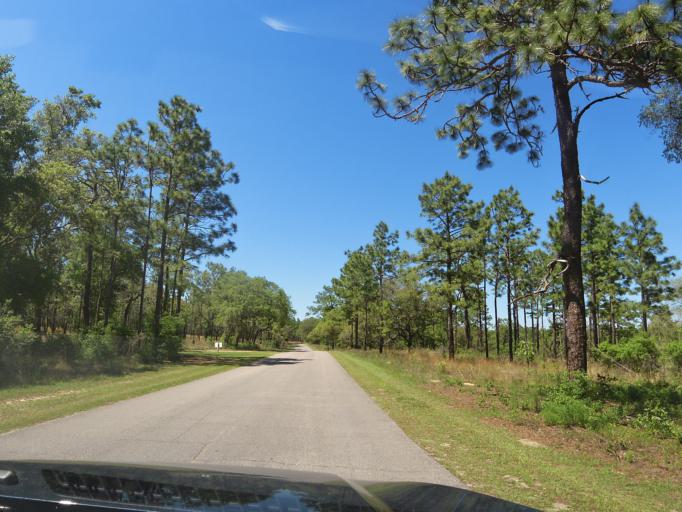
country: US
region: Florida
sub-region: Clay County
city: Keystone Heights
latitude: 29.8239
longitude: -81.9553
